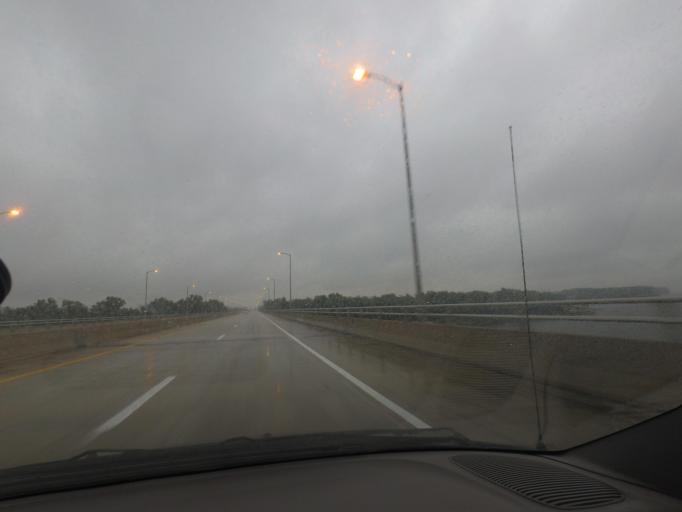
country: US
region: Missouri
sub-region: Marion County
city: Hannibal
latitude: 39.7204
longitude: -91.3572
